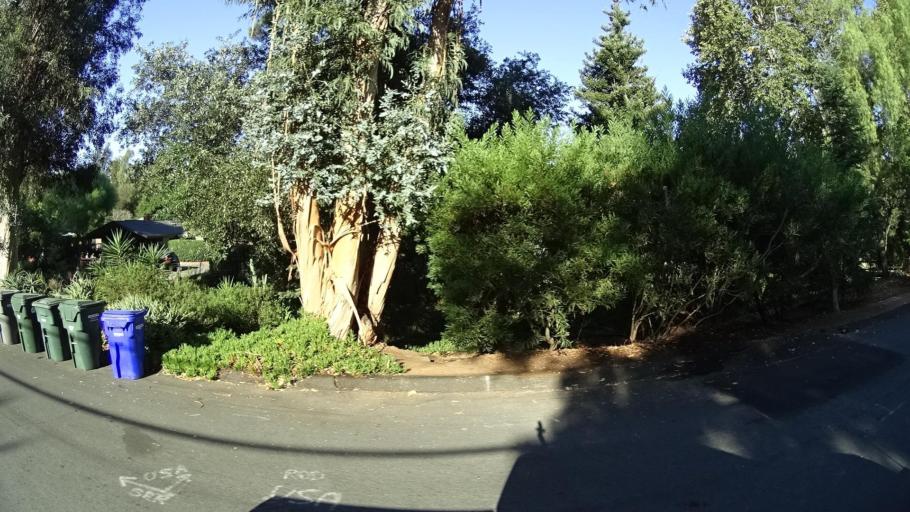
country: US
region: California
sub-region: San Diego County
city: Escondido
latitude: 33.0741
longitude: -117.0834
